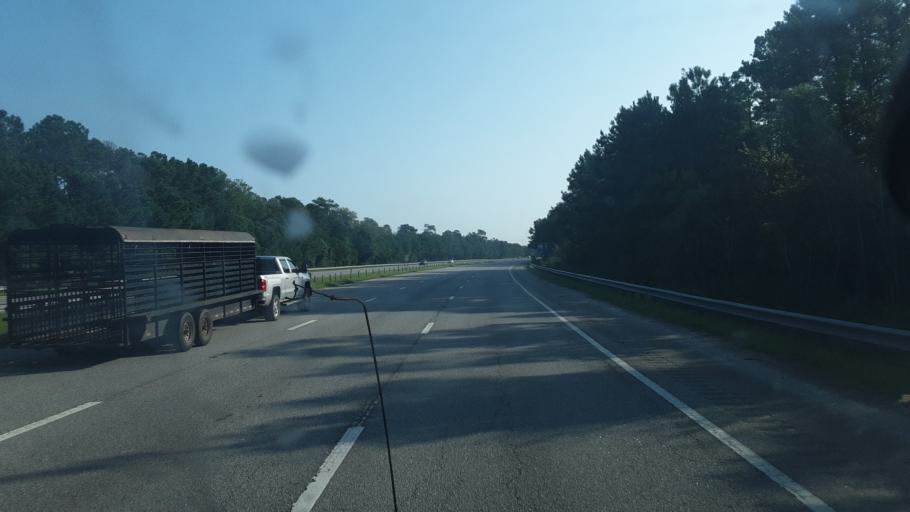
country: US
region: South Carolina
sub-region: Horry County
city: North Myrtle Beach
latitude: 33.8690
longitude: -78.6906
